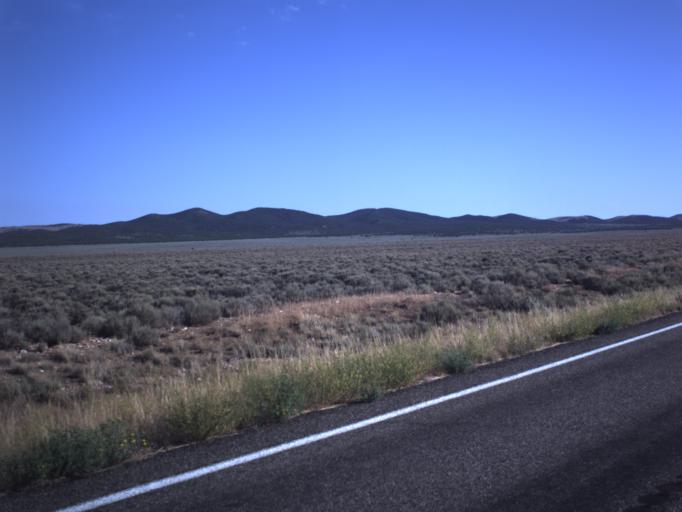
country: US
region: Utah
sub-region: Iron County
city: Enoch
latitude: 37.9762
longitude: -113.0046
